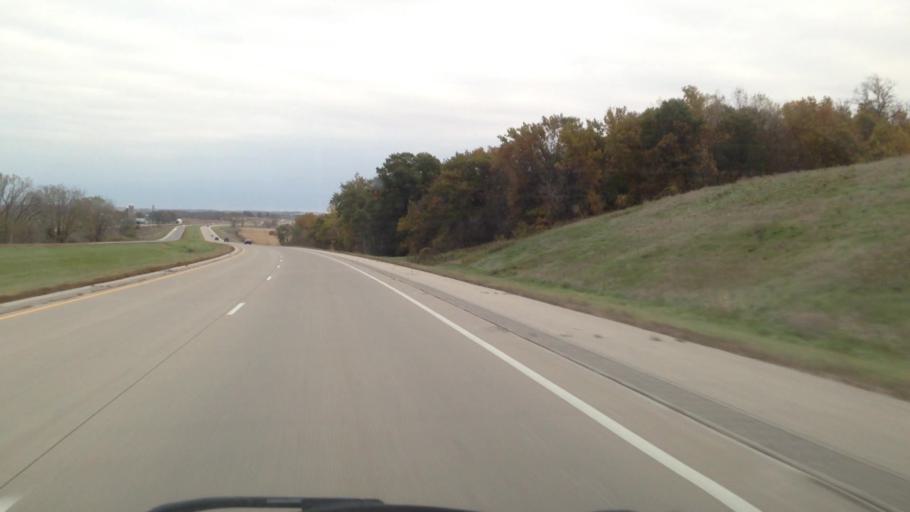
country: US
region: Minnesota
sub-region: Winona County
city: Lewiston
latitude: 43.9308
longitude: -91.9465
